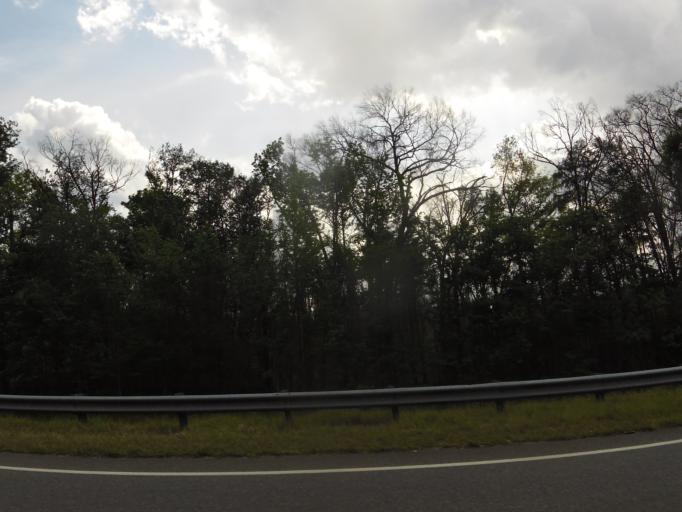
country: US
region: Florida
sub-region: Nassau County
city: Hilliard
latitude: 30.8150
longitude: -81.8439
